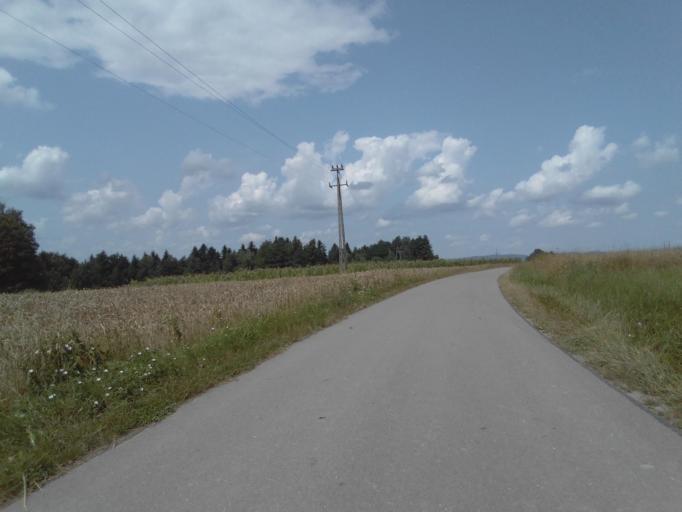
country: PL
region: Subcarpathian Voivodeship
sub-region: Powiat strzyzowski
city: Frysztak
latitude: 49.7935
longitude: 21.5996
